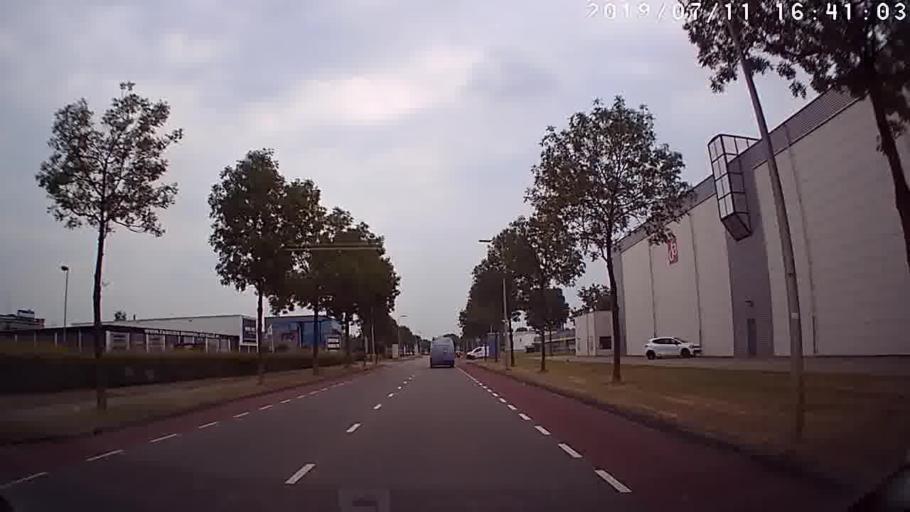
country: NL
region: Overijssel
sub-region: Gemeente Zwolle
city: Zwolle
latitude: 52.4933
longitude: 6.1256
